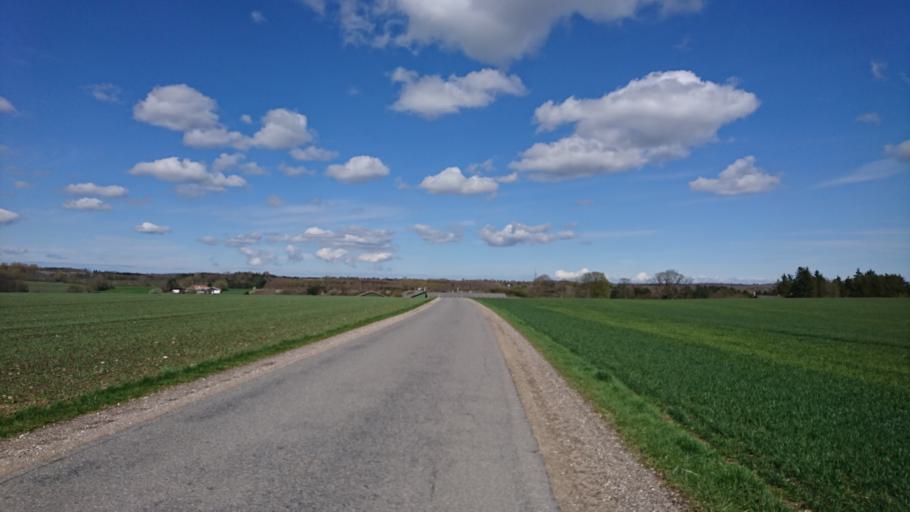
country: DK
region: Capital Region
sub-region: Egedal Kommune
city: Ganlose
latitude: 55.7710
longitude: 12.2627
